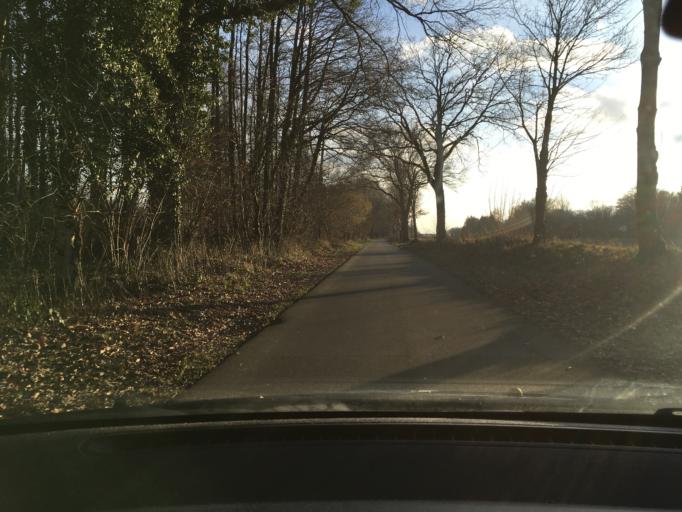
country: DE
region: Schleswig-Holstein
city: Witzeeze
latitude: 53.4576
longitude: 10.6259
